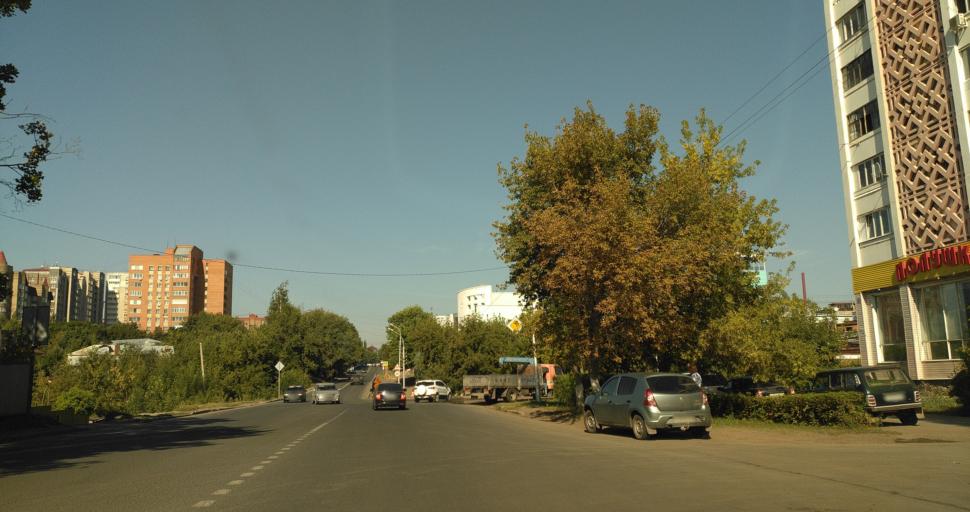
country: RU
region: Bashkortostan
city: Ufa
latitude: 54.7263
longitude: 55.9631
